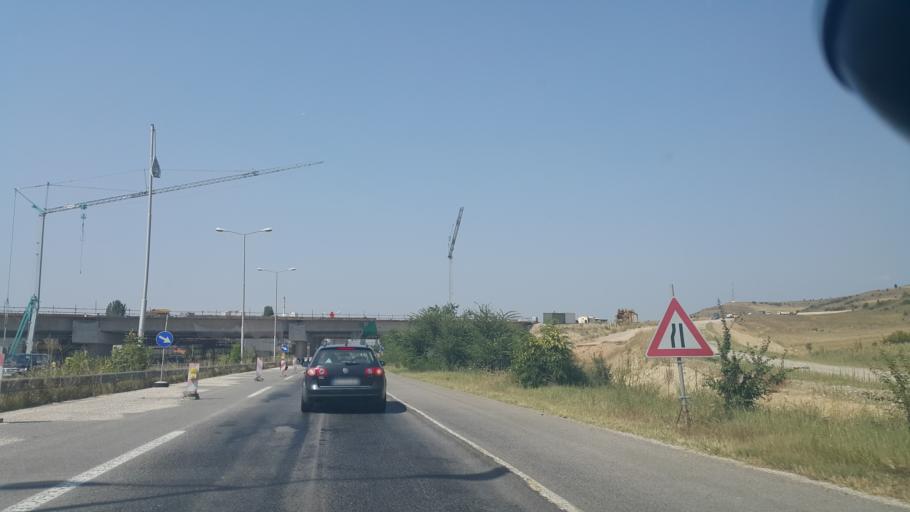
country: MK
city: Miladinovci
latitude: 41.9833
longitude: 21.6537
